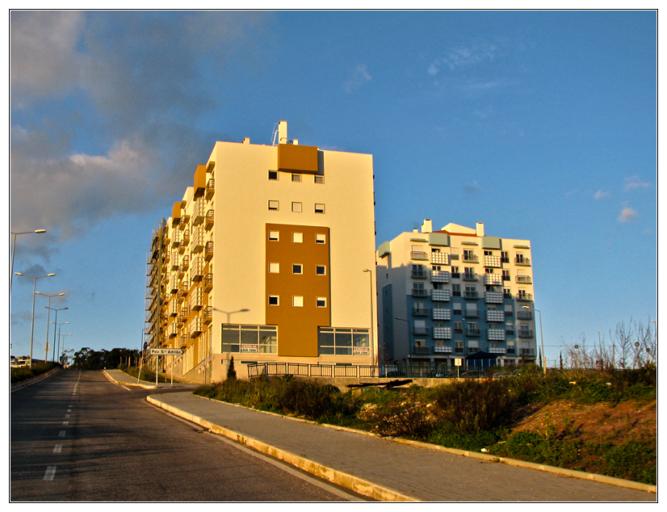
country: PT
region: Lisbon
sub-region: Odivelas
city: Povoa de Santo Adriao
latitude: 38.8044
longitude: -9.1686
